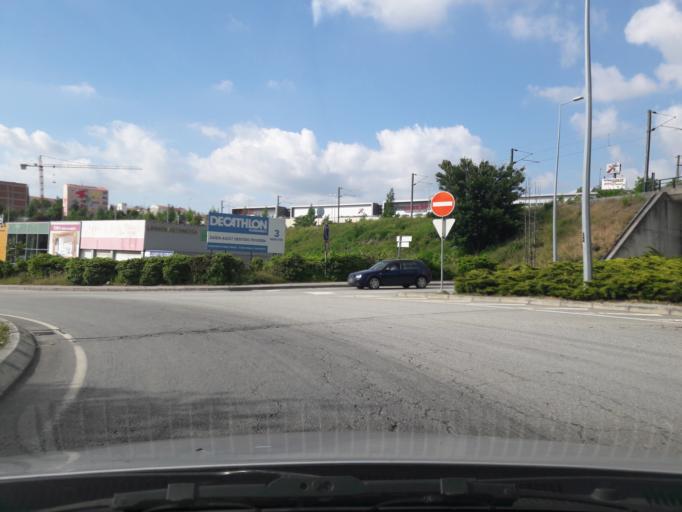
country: PT
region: Braga
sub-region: Guimaraes
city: Urgeses
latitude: 41.4228
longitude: -8.3005
